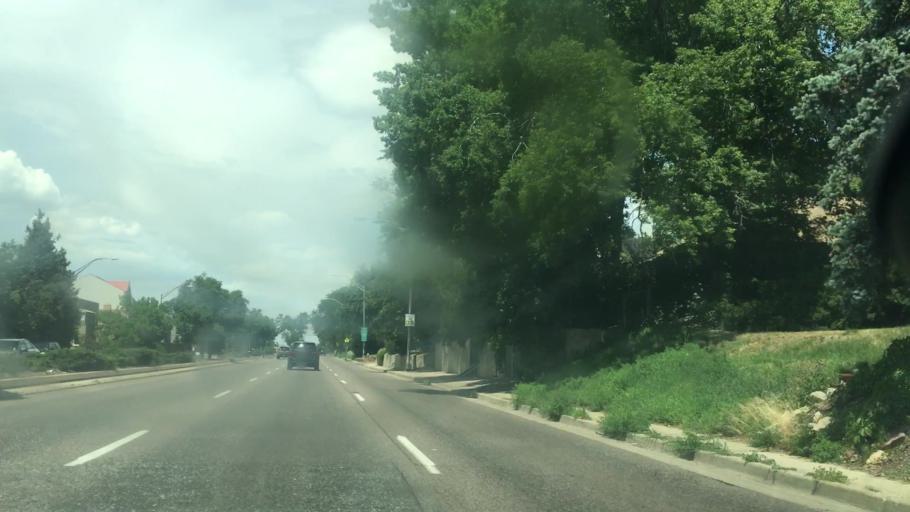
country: US
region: Colorado
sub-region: Arapahoe County
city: Glendale
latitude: 39.7186
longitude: -104.9406
